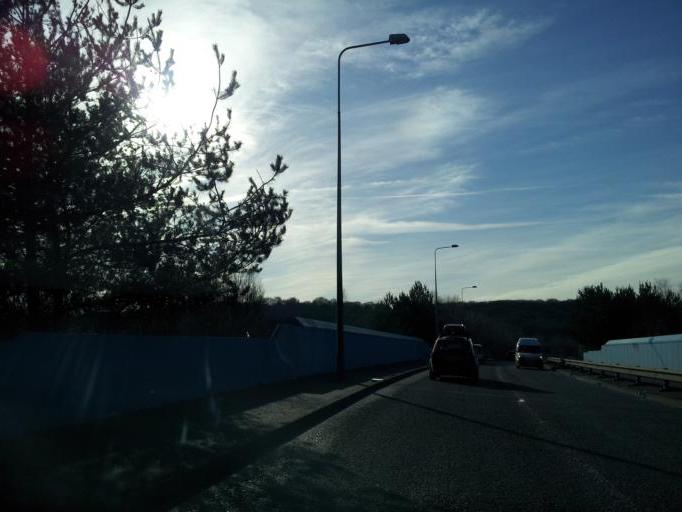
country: GB
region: England
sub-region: Staffordshire
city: Kidsgrove
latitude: 53.0565
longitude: -2.2246
